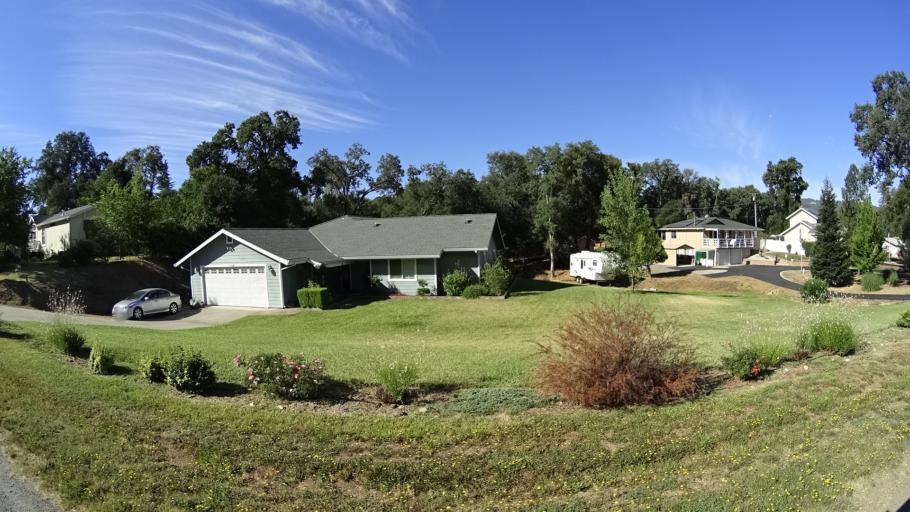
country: US
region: California
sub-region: Calaveras County
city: San Andreas
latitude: 38.1866
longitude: -120.6603
